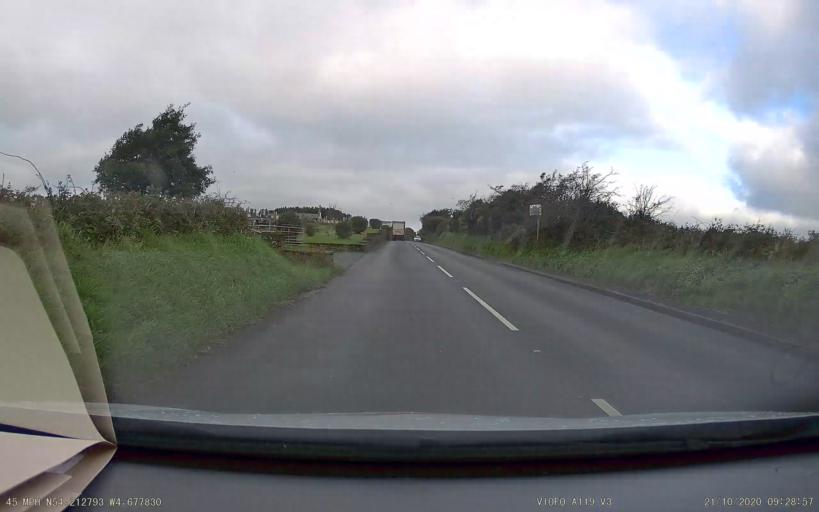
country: IM
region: Castletown
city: Castletown
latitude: 54.2128
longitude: -4.6778
